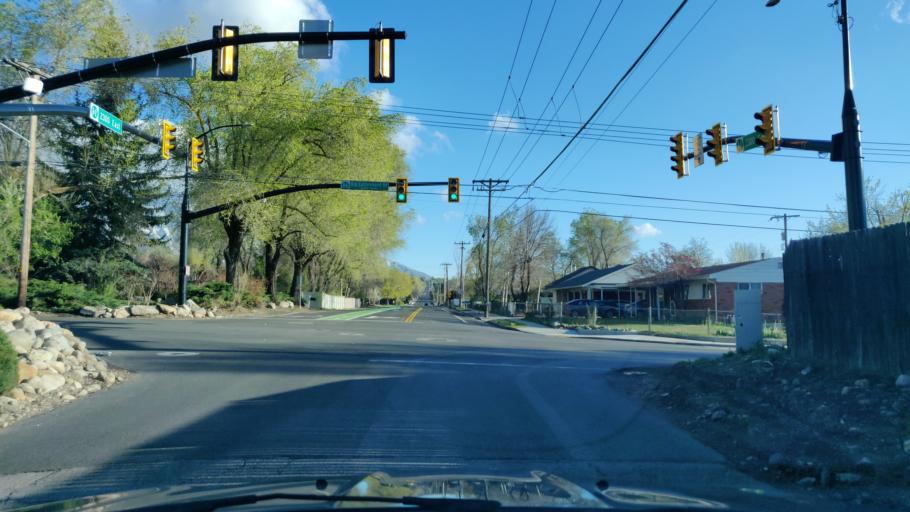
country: US
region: Utah
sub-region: Salt Lake County
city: Cottonwood Heights
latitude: 40.6387
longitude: -111.8248
